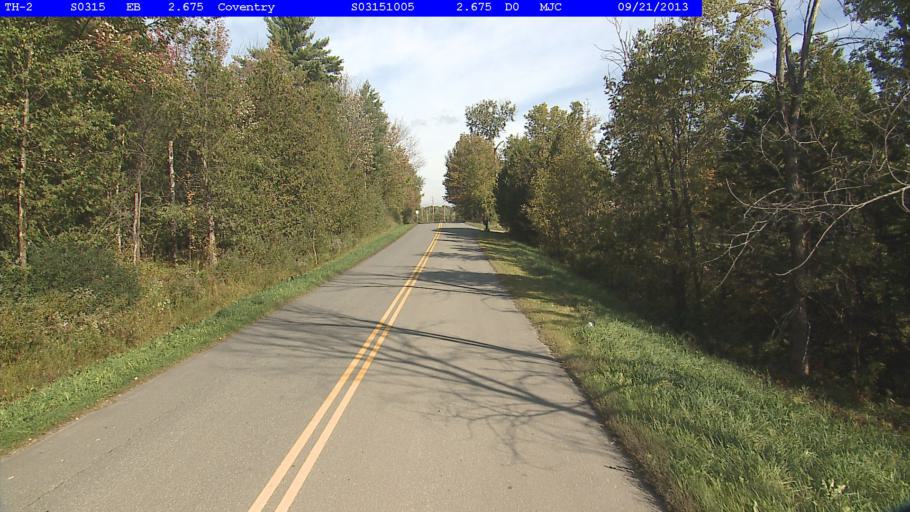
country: US
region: Vermont
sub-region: Orleans County
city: Newport
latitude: 44.8748
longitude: -72.2151
